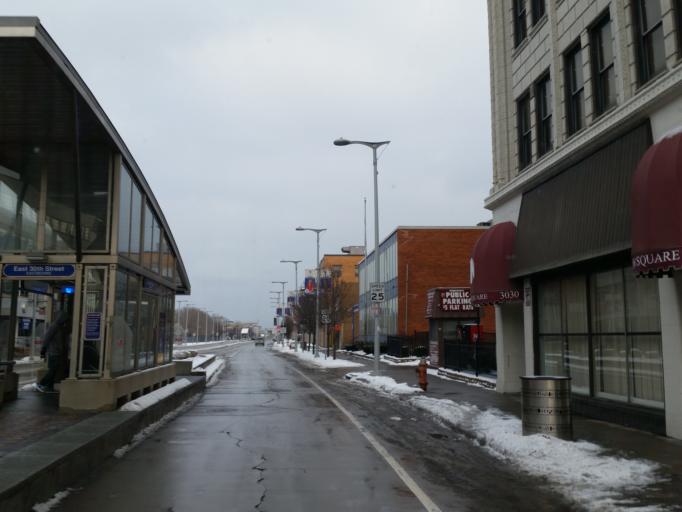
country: US
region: Ohio
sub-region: Cuyahoga County
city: Cleveland
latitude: 41.5025
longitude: -81.6670
